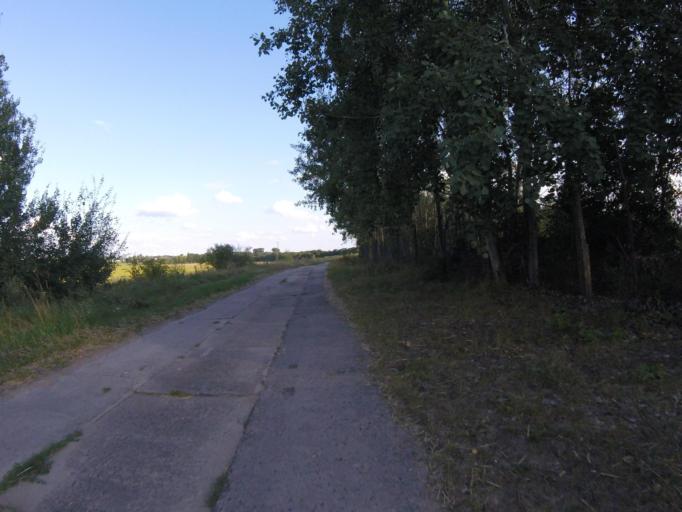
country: DE
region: Brandenburg
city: Mittenwalde
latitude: 52.2785
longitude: 13.5149
